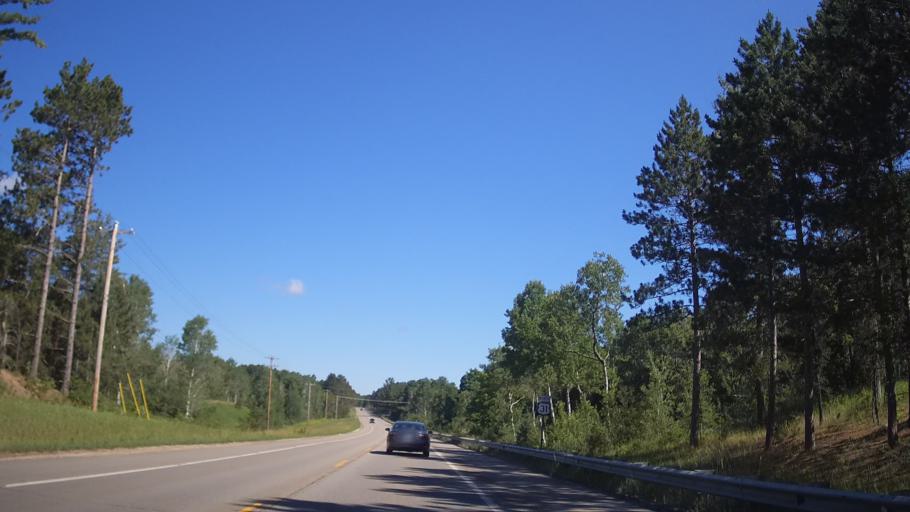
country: US
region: Michigan
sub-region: Cheboygan County
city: Indian River
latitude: 45.5363
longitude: -84.7822
